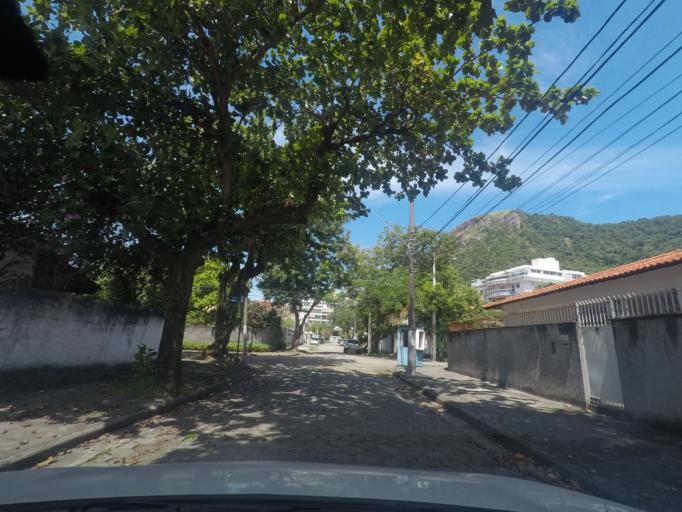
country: BR
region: Rio de Janeiro
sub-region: Niteroi
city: Niteroi
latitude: -22.9154
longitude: -43.0854
